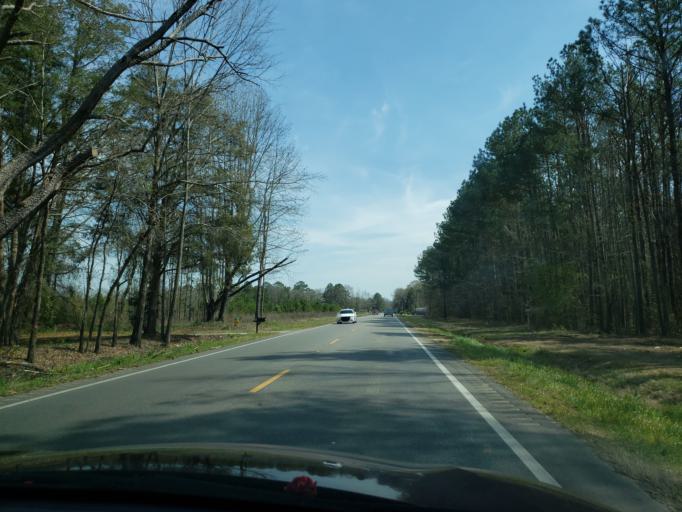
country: US
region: Alabama
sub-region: Autauga County
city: Prattville
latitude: 32.4310
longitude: -86.4954
